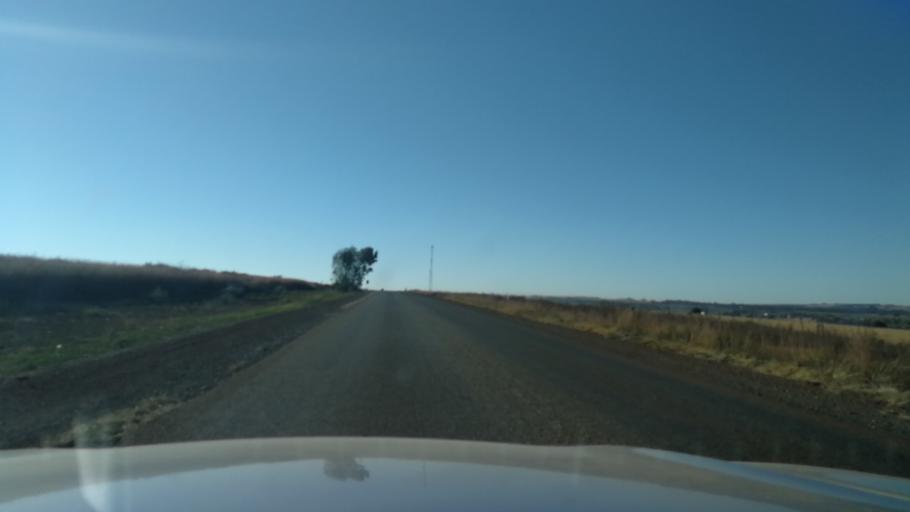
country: ZA
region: North-West
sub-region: Bojanala Platinum District Municipality
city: Rustenburg
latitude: -25.9982
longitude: 27.3034
